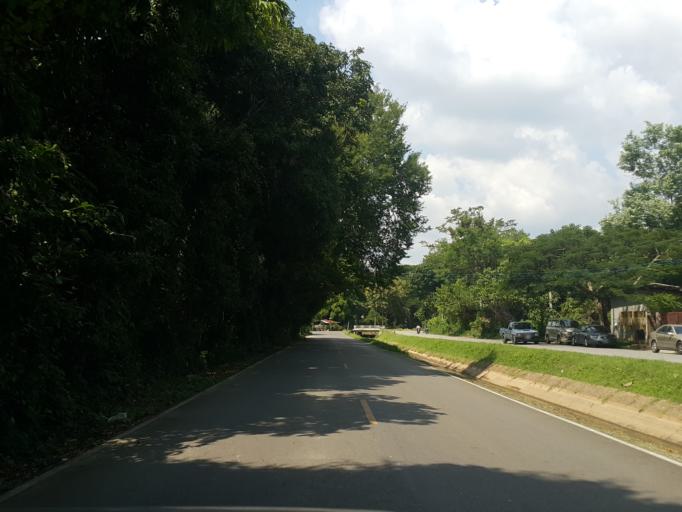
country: TH
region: Chiang Mai
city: Hang Dong
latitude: 18.7029
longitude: 98.9153
